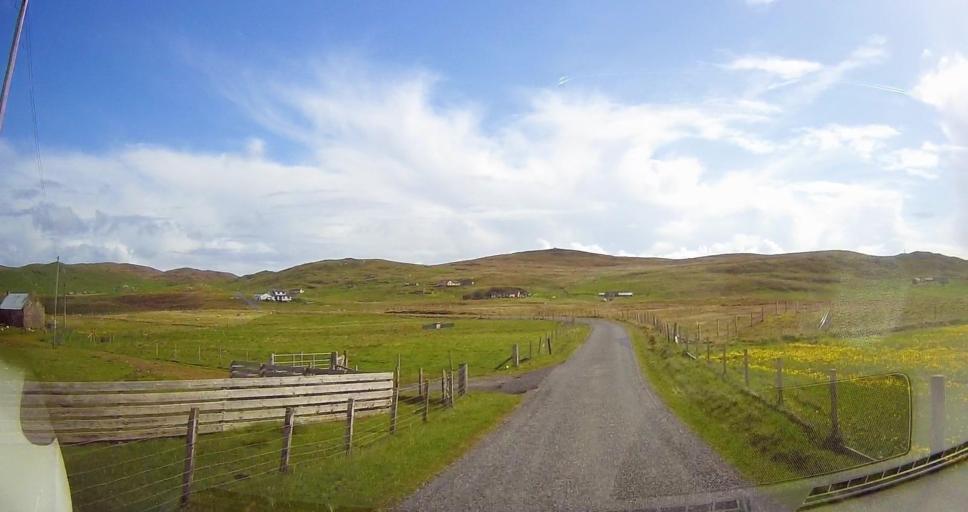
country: GB
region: Scotland
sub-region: Shetland Islands
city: Lerwick
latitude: 60.5902
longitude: -1.3327
